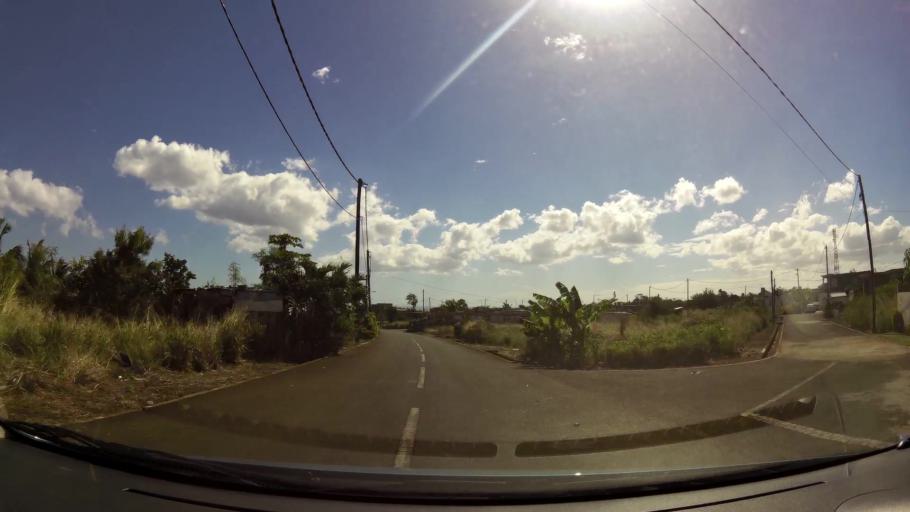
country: MU
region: Black River
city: Cascavelle
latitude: -20.2693
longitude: 57.4143
